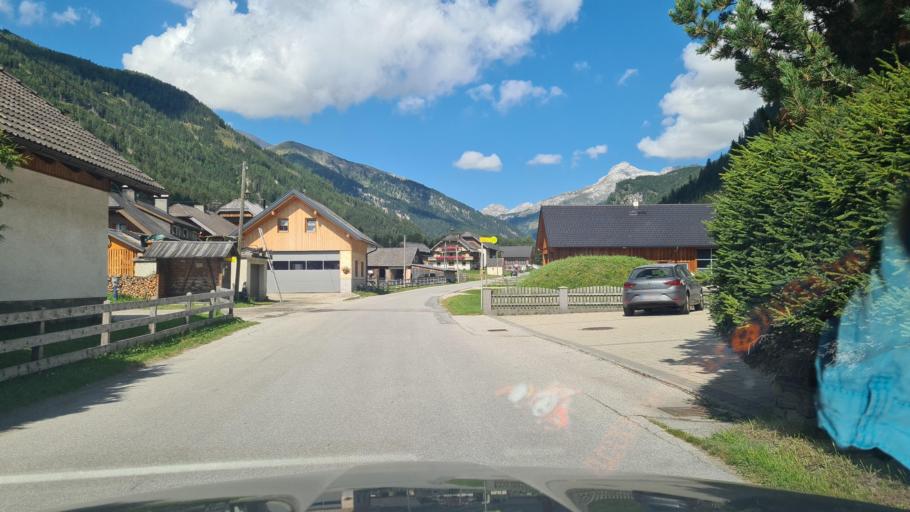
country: AT
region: Salzburg
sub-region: Politischer Bezirk Tamsweg
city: Zederhaus
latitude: 47.1613
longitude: 13.4852
